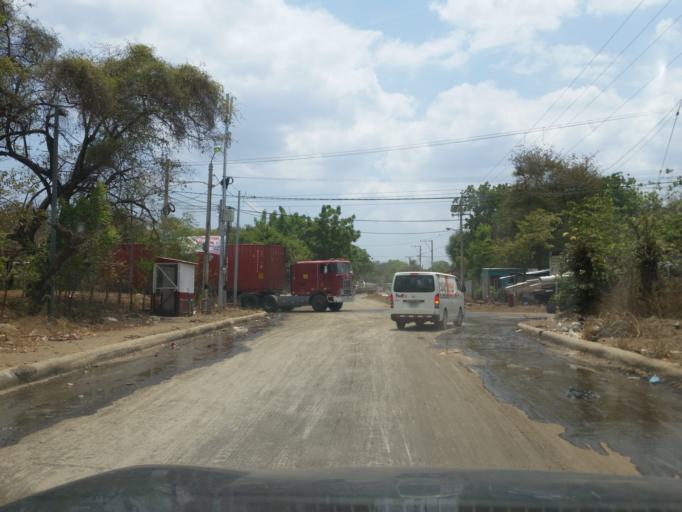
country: NI
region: Managua
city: Managua
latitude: 12.1231
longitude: -86.1656
